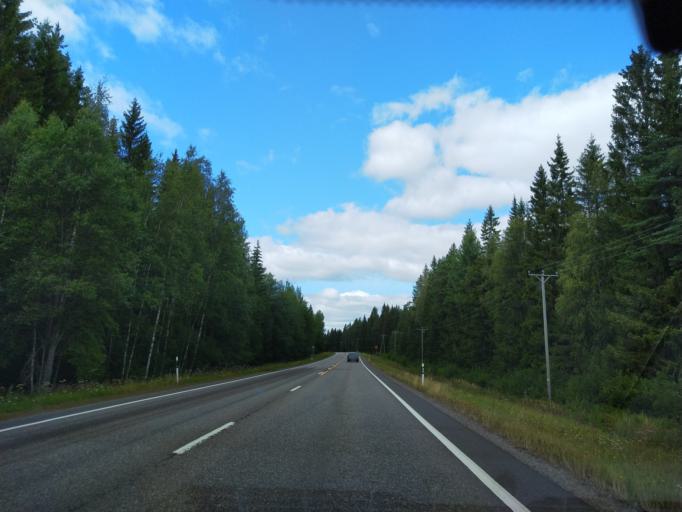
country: FI
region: Haeme
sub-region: Haemeenlinna
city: Renko
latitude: 60.7575
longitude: 24.2966
